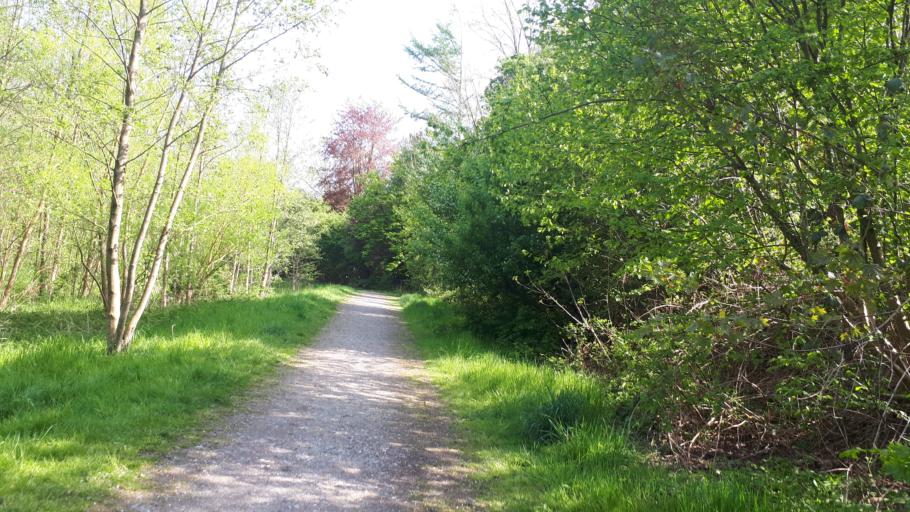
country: DE
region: North Rhine-Westphalia
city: Castrop-Rauxel
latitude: 51.5438
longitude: 7.3209
